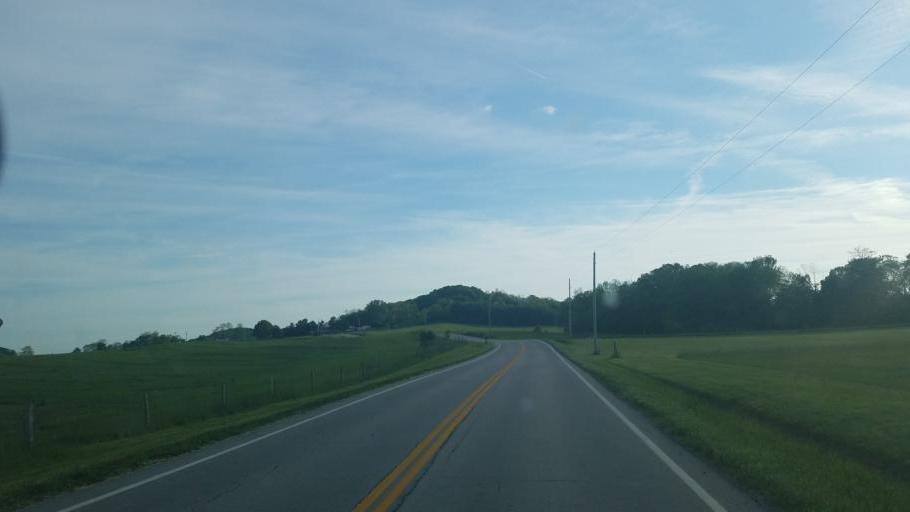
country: US
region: Ohio
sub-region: Ross County
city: Frankfort
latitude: 39.4215
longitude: -83.2662
